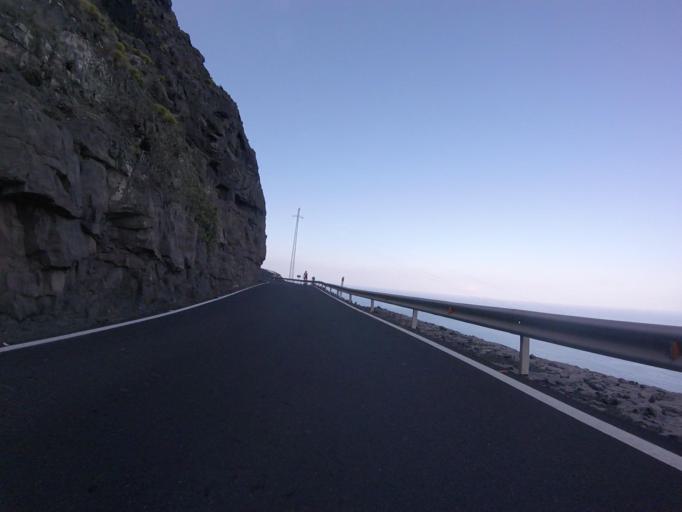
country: ES
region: Canary Islands
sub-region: Provincia de Las Palmas
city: Agaete
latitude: 28.0691
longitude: -15.7205
